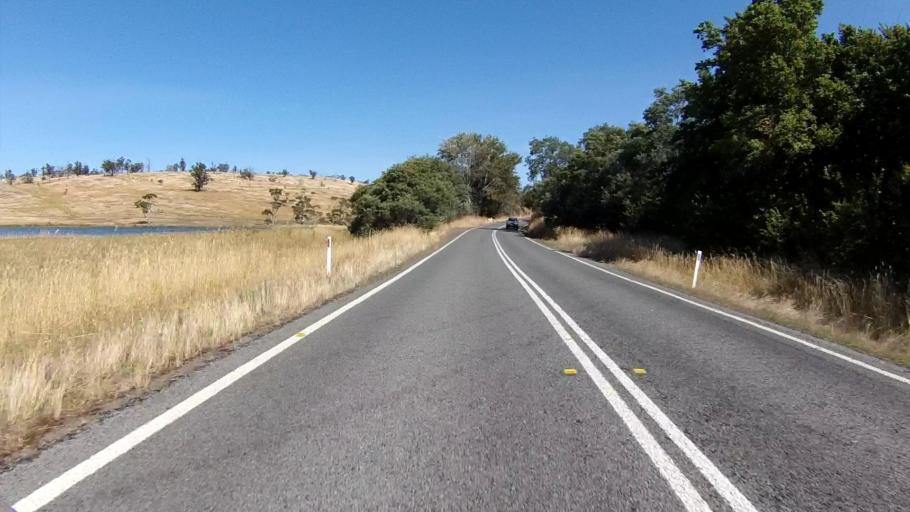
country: AU
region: Tasmania
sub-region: Sorell
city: Sorell
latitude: -42.4896
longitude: 147.9339
